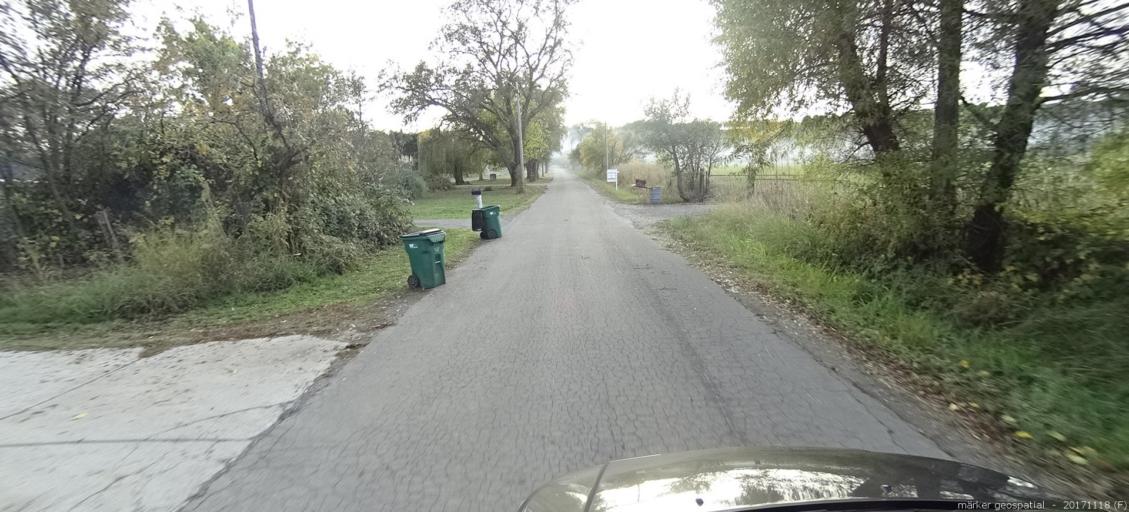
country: US
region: California
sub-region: Shasta County
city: Anderson
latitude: 40.4544
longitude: -122.3212
